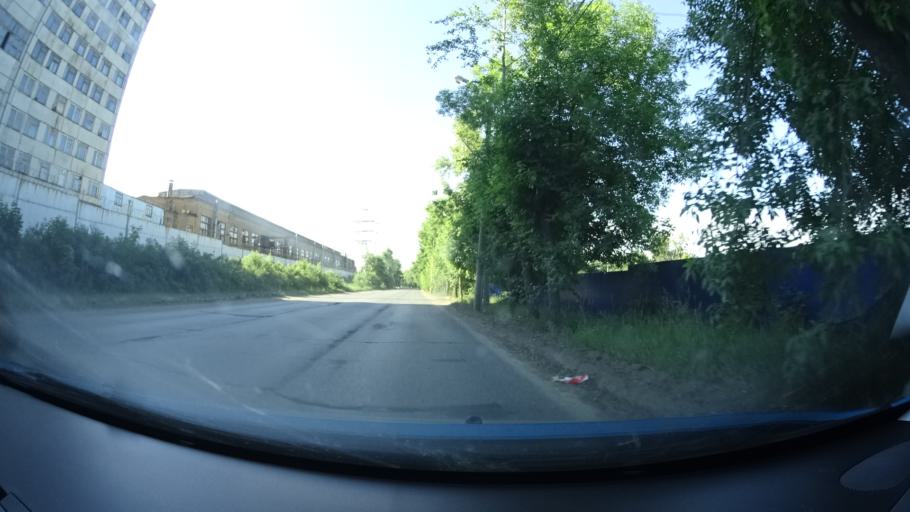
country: RU
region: Bashkortostan
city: Ufa
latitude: 54.8409
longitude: 56.0755
